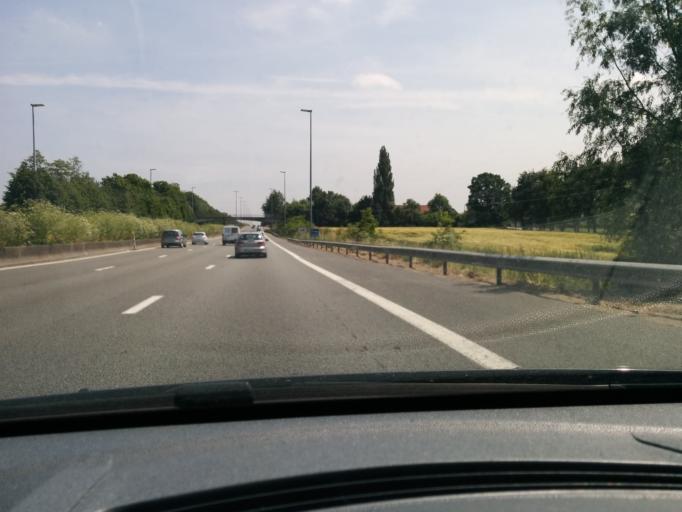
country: BE
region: Flanders
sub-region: Provincie Oost-Vlaanderen
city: Sint-Lievens-Houtem
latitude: 50.9660
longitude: 3.8521
